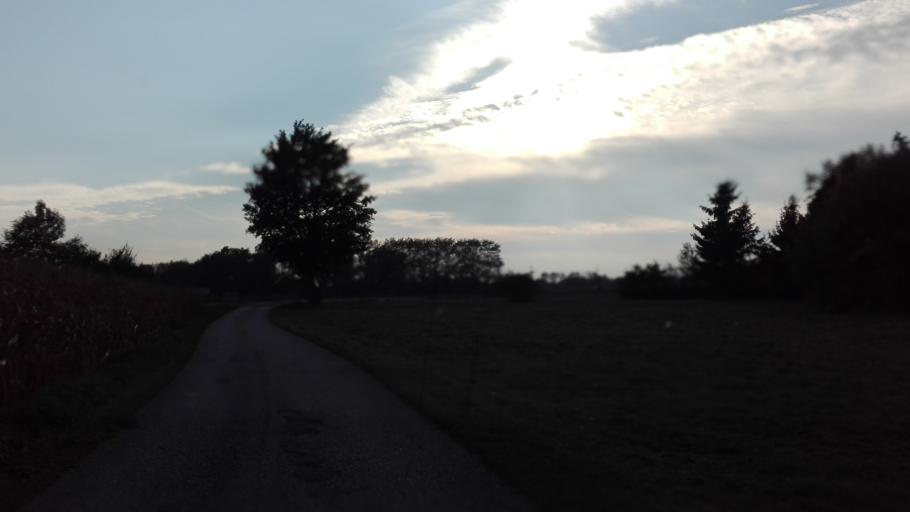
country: AT
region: Upper Austria
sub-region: Politischer Bezirk Perg
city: Perg
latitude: 48.2355
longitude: 14.6581
